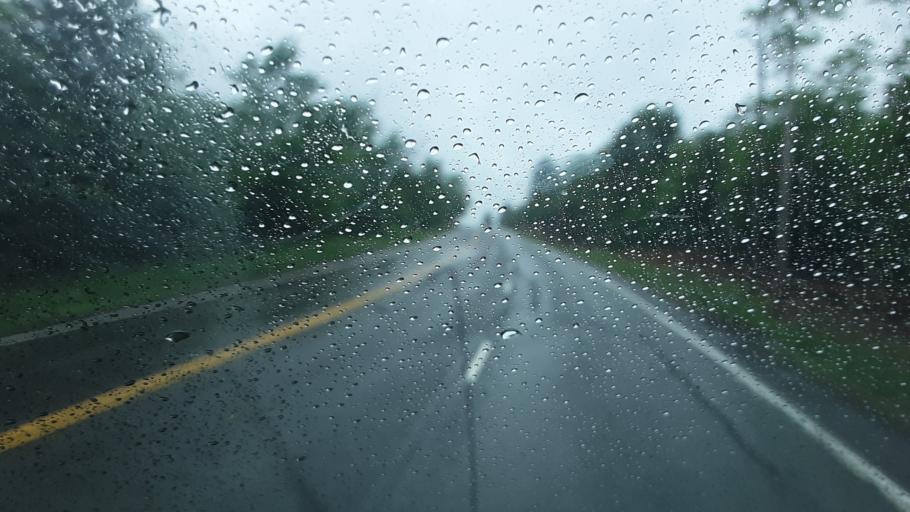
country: US
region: Maine
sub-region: Penobscot County
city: Patten
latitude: 46.1760
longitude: -68.3368
